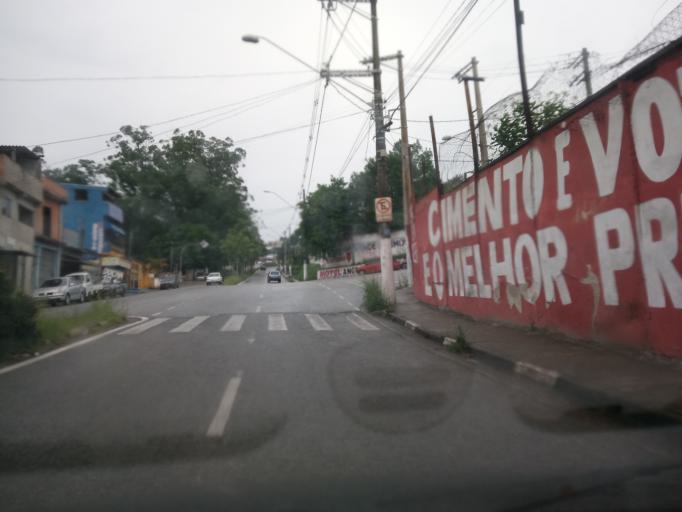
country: BR
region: Sao Paulo
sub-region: Sao Bernardo Do Campo
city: Sao Bernardo do Campo
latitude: -23.7695
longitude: -46.5958
